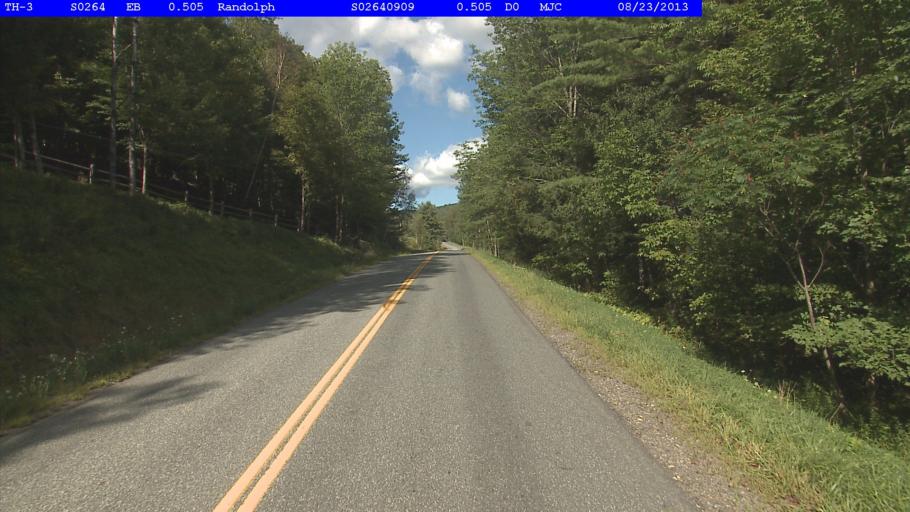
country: US
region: Vermont
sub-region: Orange County
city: Chelsea
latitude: 43.9373
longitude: -72.5446
